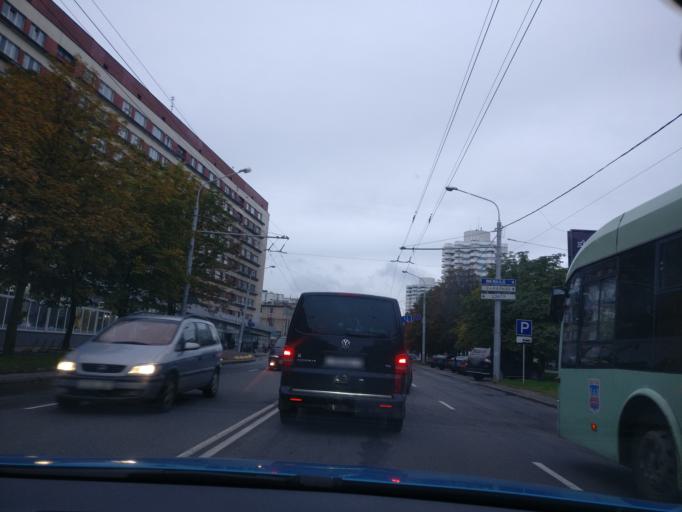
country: BY
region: Minsk
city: Minsk
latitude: 53.9210
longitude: 27.5699
